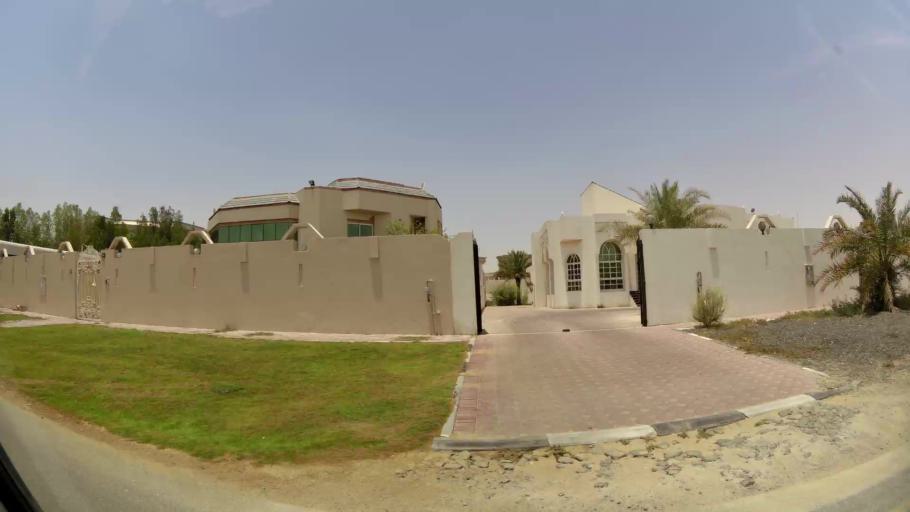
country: AE
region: Ash Shariqah
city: Sharjah
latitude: 25.2364
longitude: 55.4637
